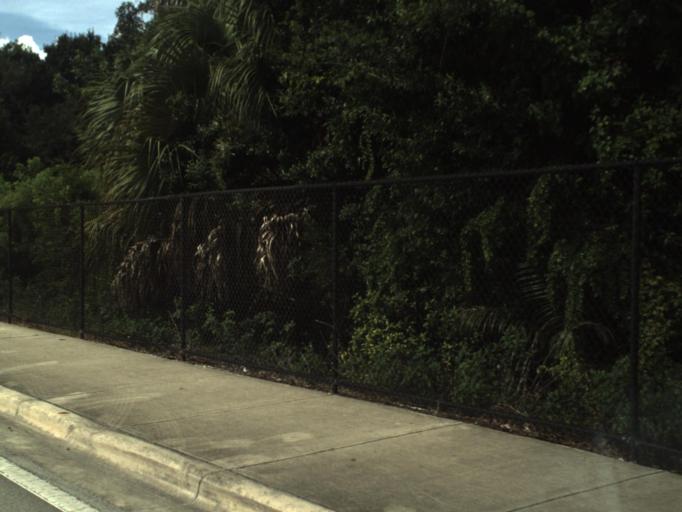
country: US
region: Florida
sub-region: Broward County
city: Dania Beach
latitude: 26.0854
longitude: -80.1467
